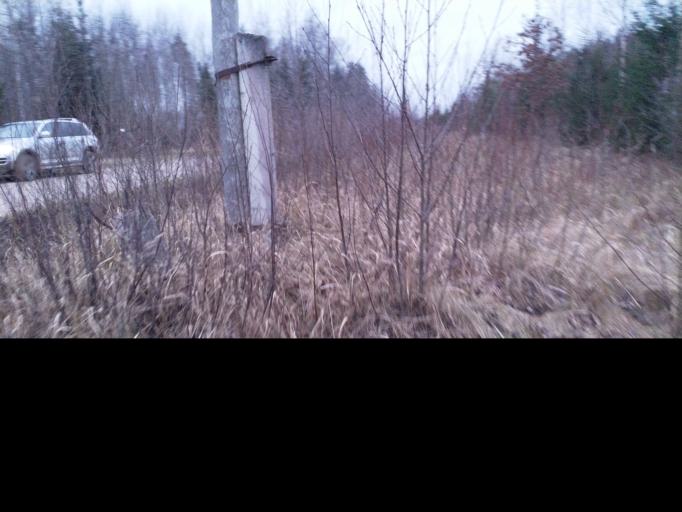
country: LV
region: Alsunga
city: Alsunga
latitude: 56.9560
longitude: 21.5385
